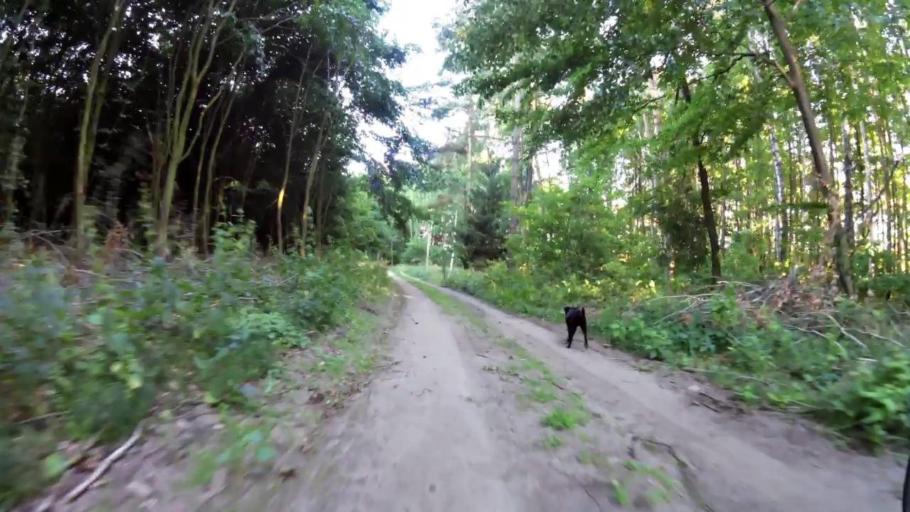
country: PL
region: West Pomeranian Voivodeship
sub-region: Powiat lobeski
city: Lobez
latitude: 53.7426
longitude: 15.6369
